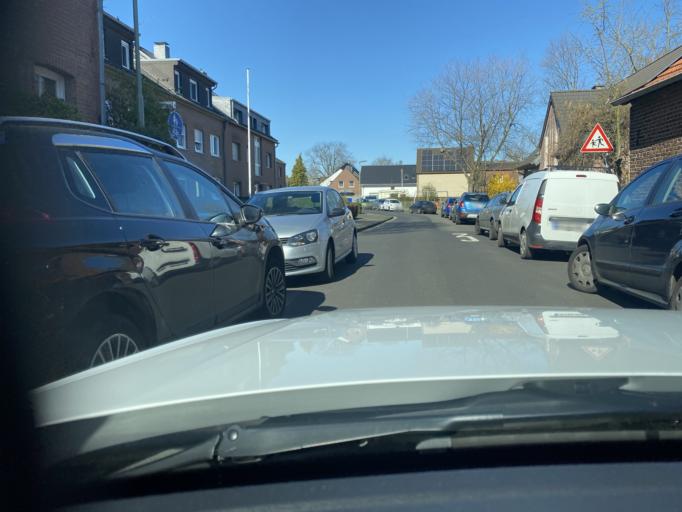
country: DE
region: North Rhine-Westphalia
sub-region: Regierungsbezirk Dusseldorf
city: Neubrueck
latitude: 51.1588
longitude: 6.6657
